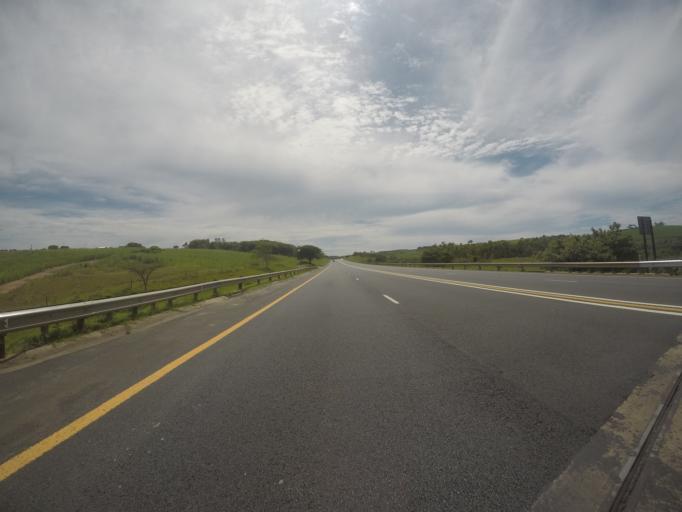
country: ZA
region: KwaZulu-Natal
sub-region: iLembe District Municipality
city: Mandeni
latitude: -29.1689
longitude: 31.5220
